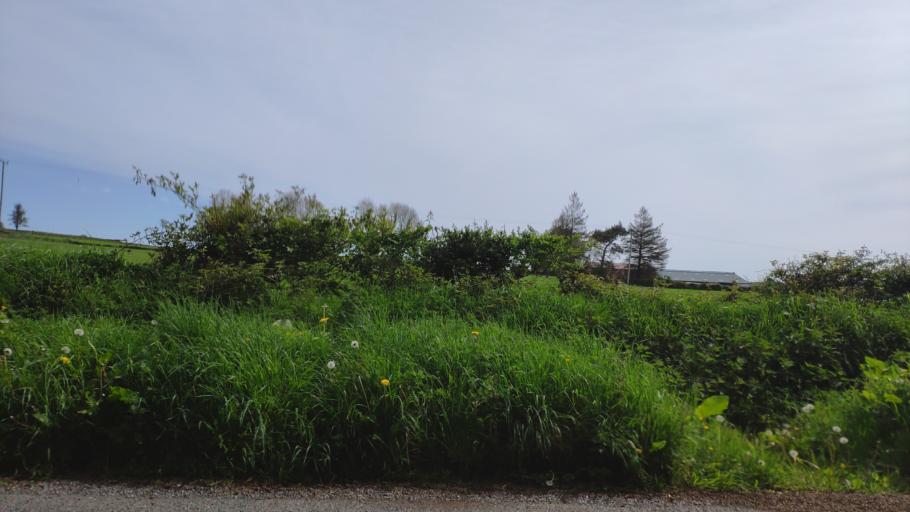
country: IE
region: Munster
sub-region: County Cork
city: Blarney
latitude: 51.9534
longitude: -8.5048
